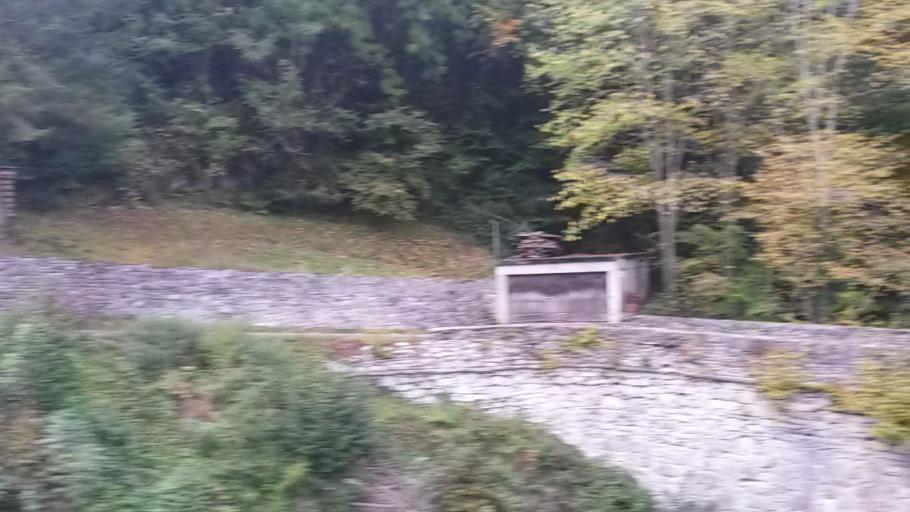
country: CH
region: Valais
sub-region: Monthey District
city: Troistorrents
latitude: 46.2185
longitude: 6.9035
